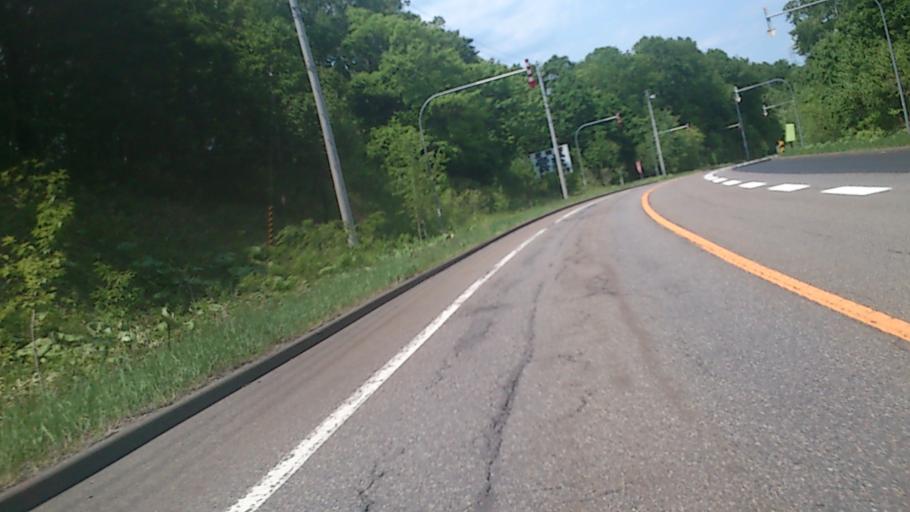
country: JP
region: Hokkaido
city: Otofuke
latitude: 43.2312
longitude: 143.5260
